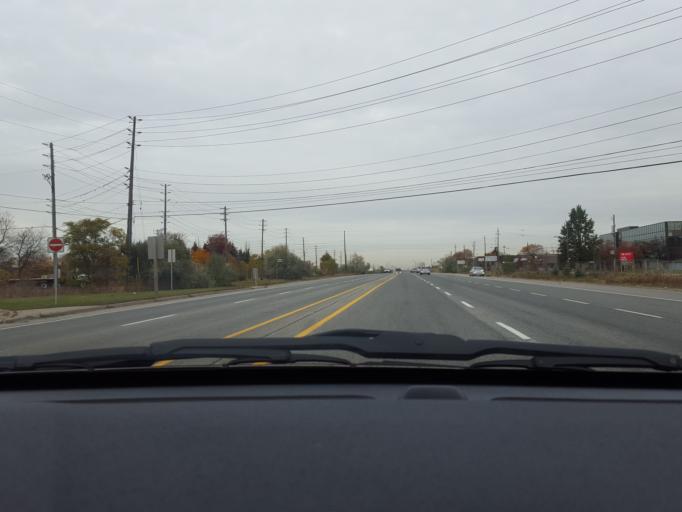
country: CA
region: Ontario
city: Etobicoke
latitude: 43.6920
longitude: -79.5837
